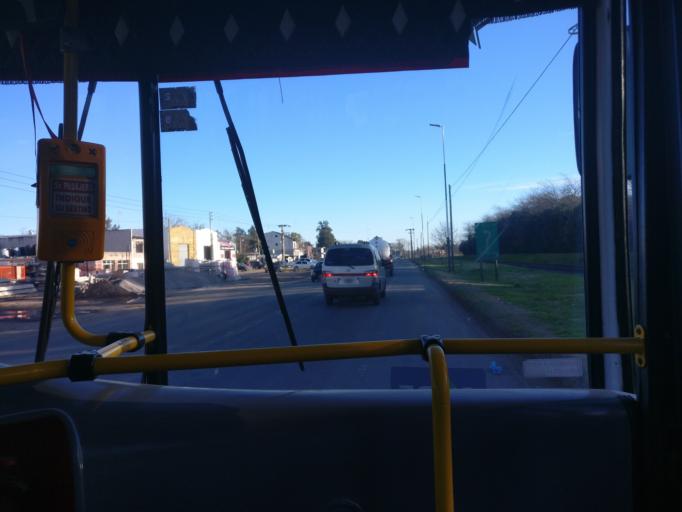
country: AR
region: Buenos Aires
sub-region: Partido de Ezeiza
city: Ezeiza
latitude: -34.9162
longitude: -58.6020
